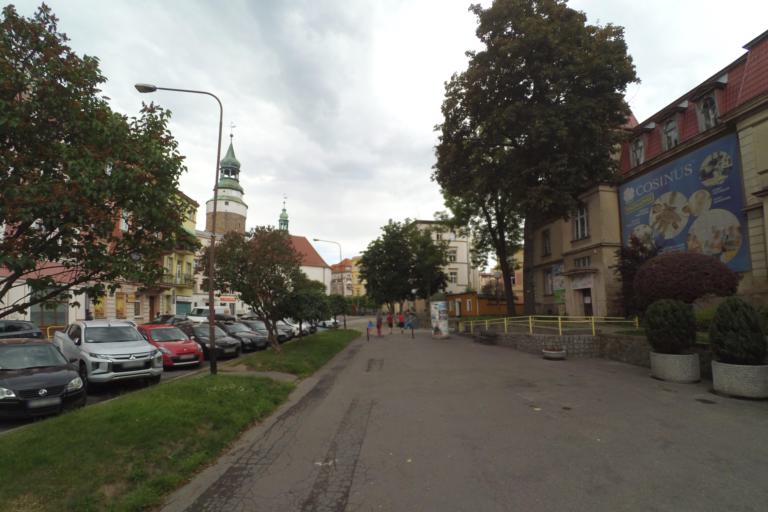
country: PL
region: Lower Silesian Voivodeship
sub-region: Jelenia Gora
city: Jelenia Gora
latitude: 50.9023
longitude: 15.7374
